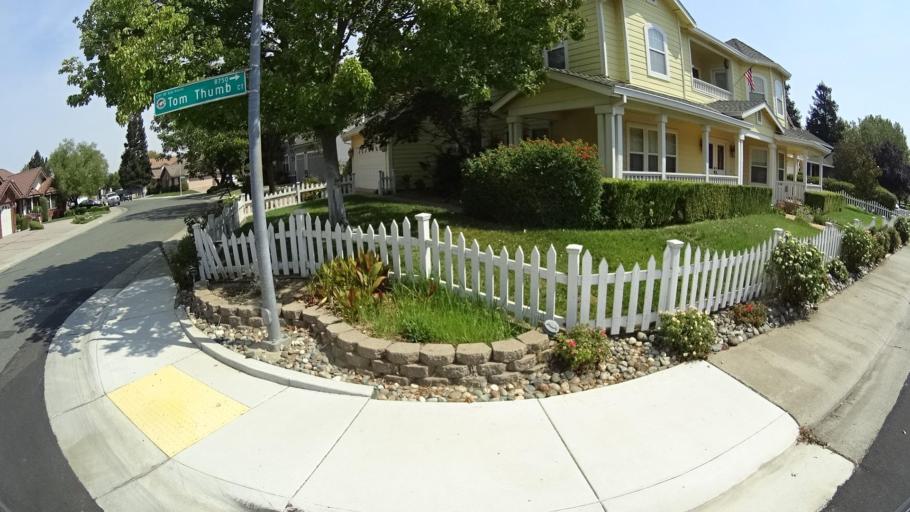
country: US
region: California
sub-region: Sacramento County
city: Elk Grove
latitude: 38.4263
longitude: -121.3788
